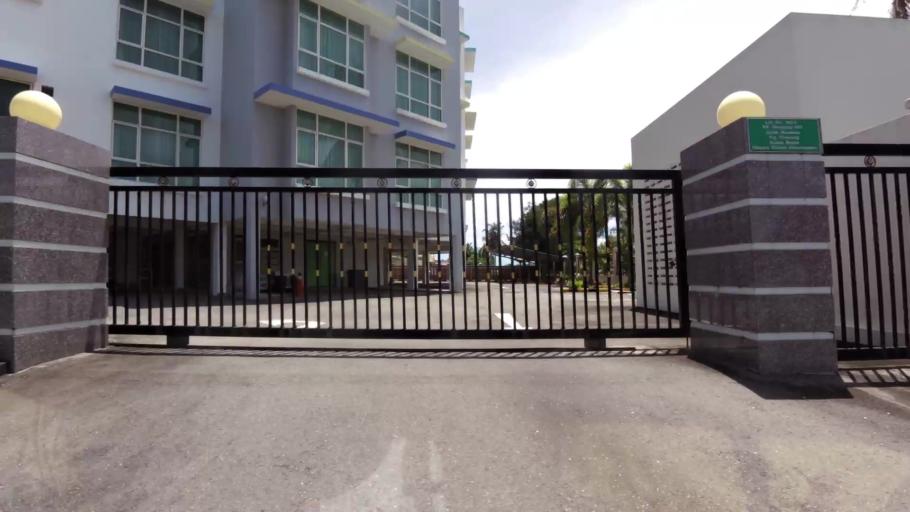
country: BN
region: Belait
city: Kuala Belait
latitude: 4.5938
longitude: 114.2393
